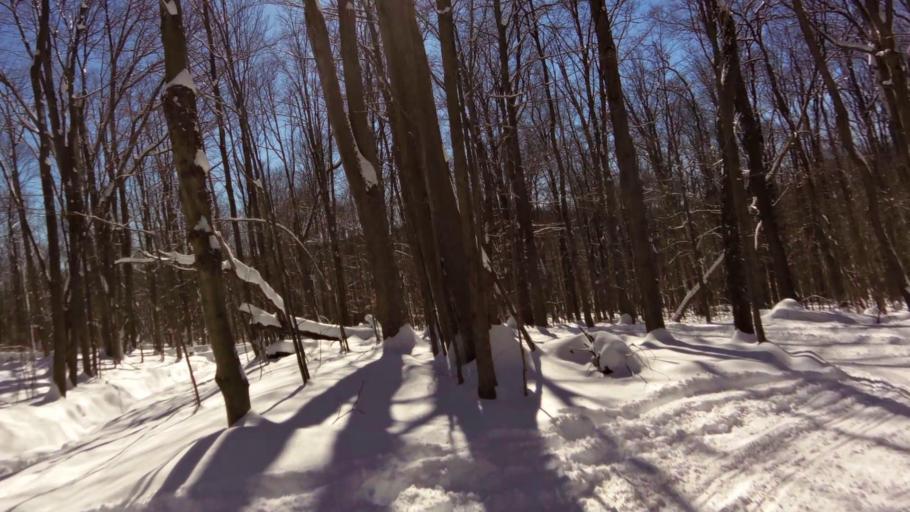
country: US
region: New York
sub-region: Chautauqua County
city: Mayville
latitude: 42.2061
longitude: -79.5349
